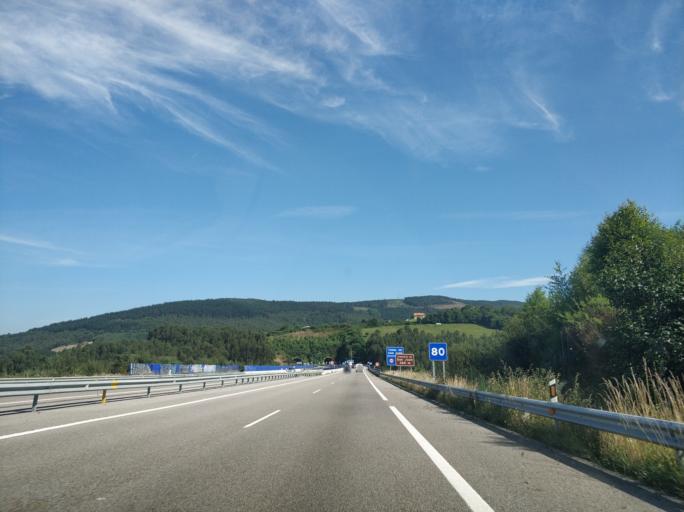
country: ES
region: Asturias
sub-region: Province of Asturias
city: Cudillero
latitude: 43.5467
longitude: -6.1605
